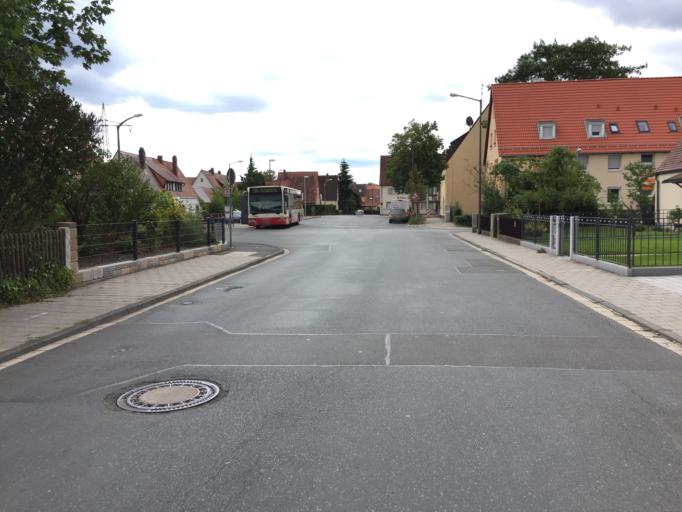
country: DE
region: Bavaria
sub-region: Regierungsbezirk Mittelfranken
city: Erlangen
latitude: 49.5646
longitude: 11.0022
